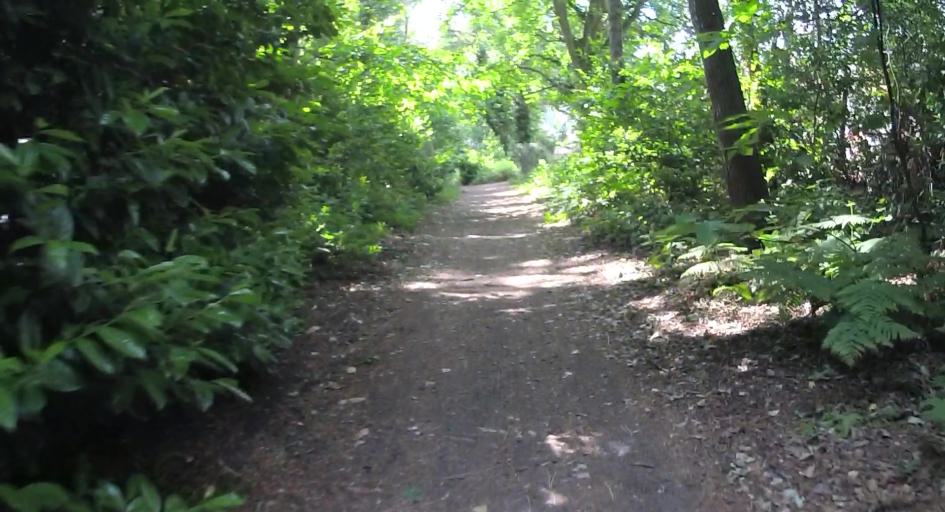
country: GB
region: England
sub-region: Bracknell Forest
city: Crowthorne
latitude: 51.3820
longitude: -0.8019
